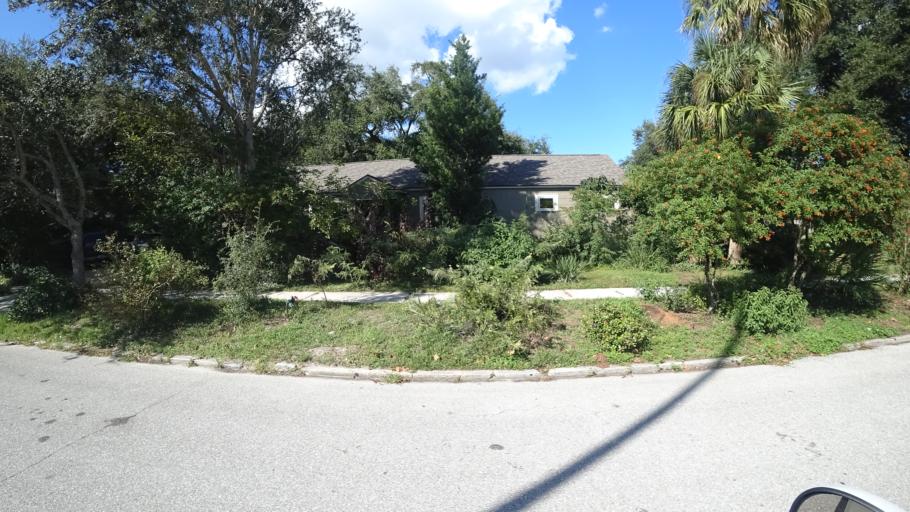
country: US
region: Florida
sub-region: Manatee County
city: Bradenton
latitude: 27.4838
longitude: -82.5847
